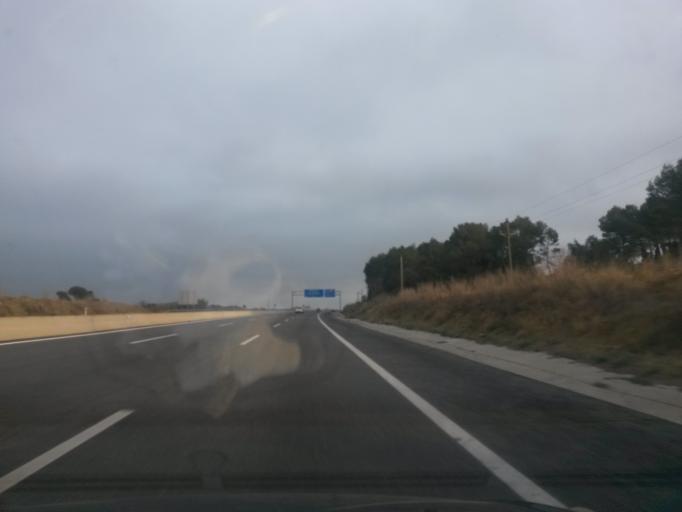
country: ES
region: Catalonia
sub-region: Provincia de Girona
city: Vilademuls
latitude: 42.1196
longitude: 2.9123
